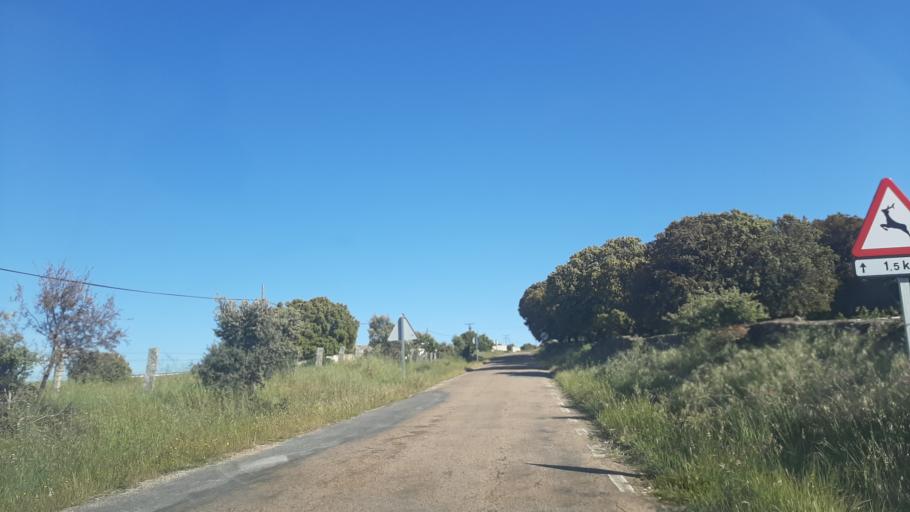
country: ES
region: Castille and Leon
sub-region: Provincia de Salamanca
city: Guijuelo
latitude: 40.5429
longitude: -5.6629
